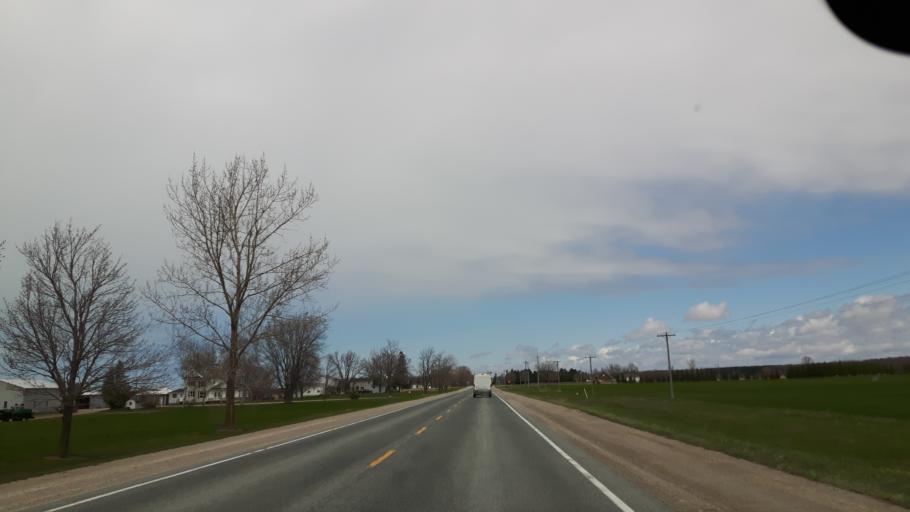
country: CA
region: Ontario
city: Bluewater
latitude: 43.4877
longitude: -81.6970
